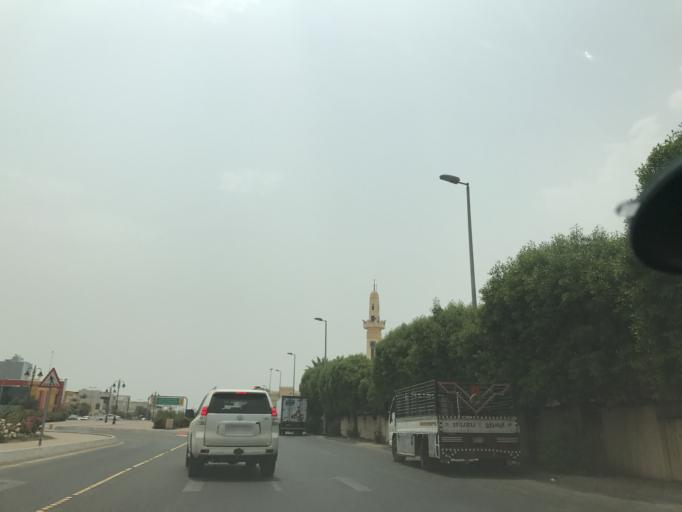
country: SA
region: Makkah
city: Jeddah
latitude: 21.5579
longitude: 39.1708
